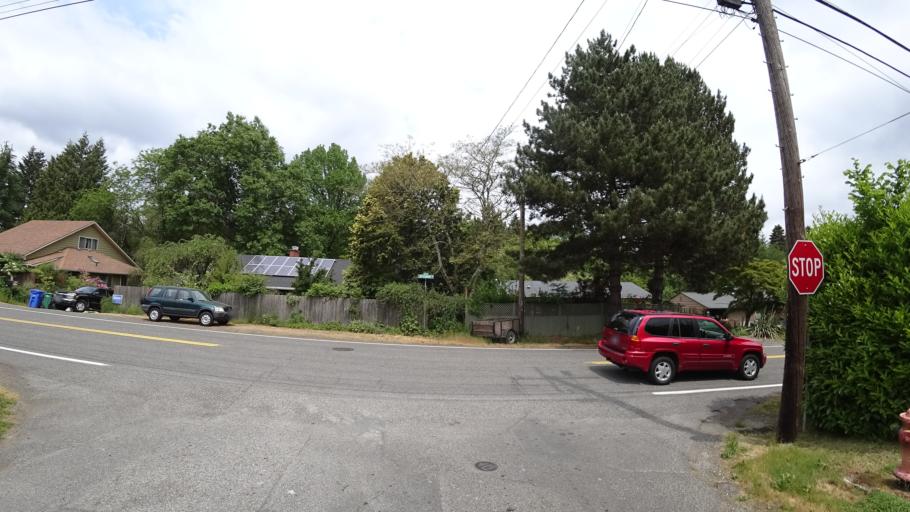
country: US
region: Oregon
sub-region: Washington County
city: Garden Home-Whitford
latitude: 45.4762
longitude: -122.7325
